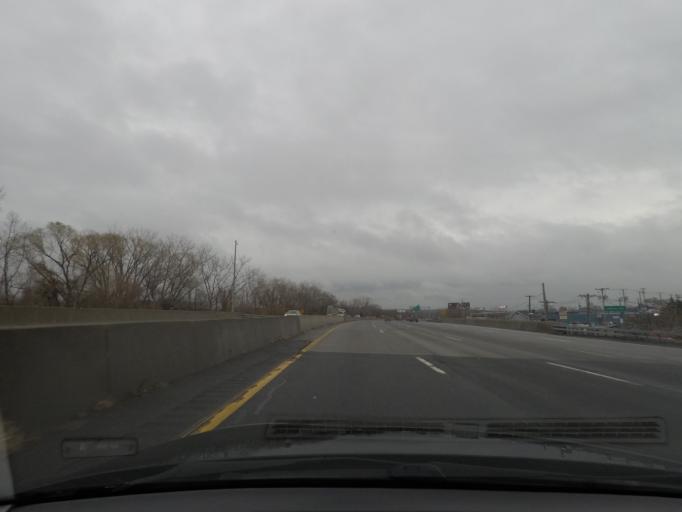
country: US
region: New York
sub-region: Albany County
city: Roessleville
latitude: 42.6873
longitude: -73.7987
